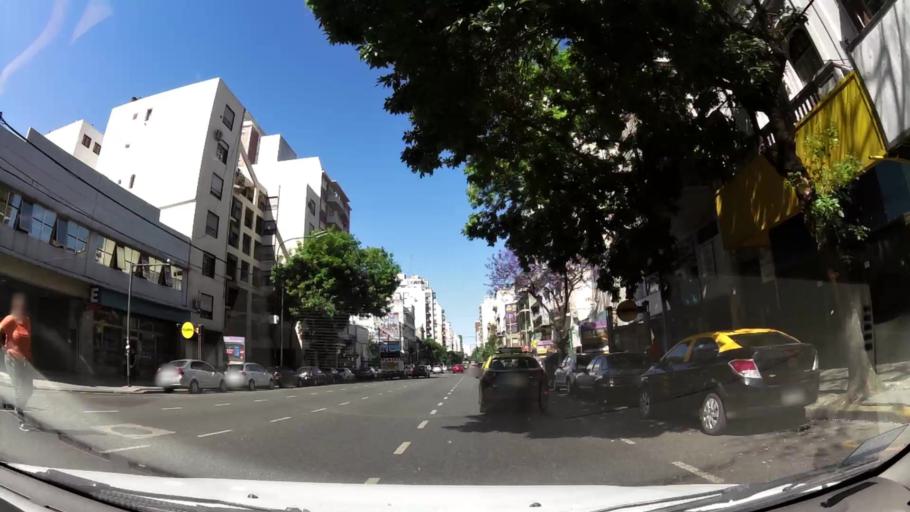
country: AR
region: Buenos Aires F.D.
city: Buenos Aires
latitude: -34.6239
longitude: -58.4031
